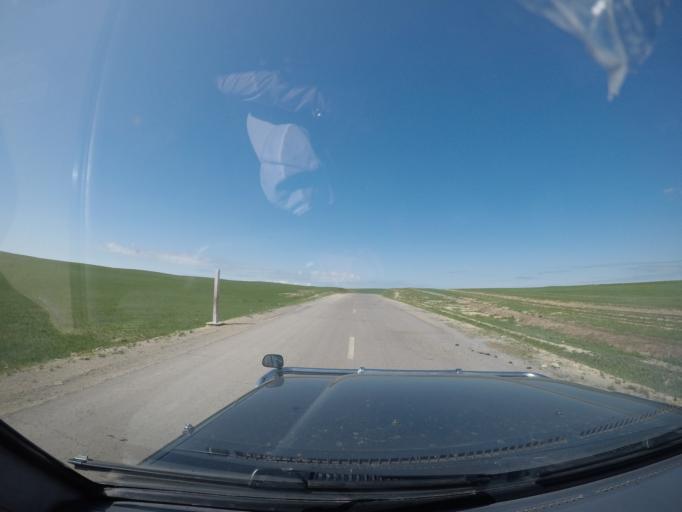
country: MN
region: Suhbaatar
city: Bayasgalant
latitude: 47.3542
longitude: 111.6692
